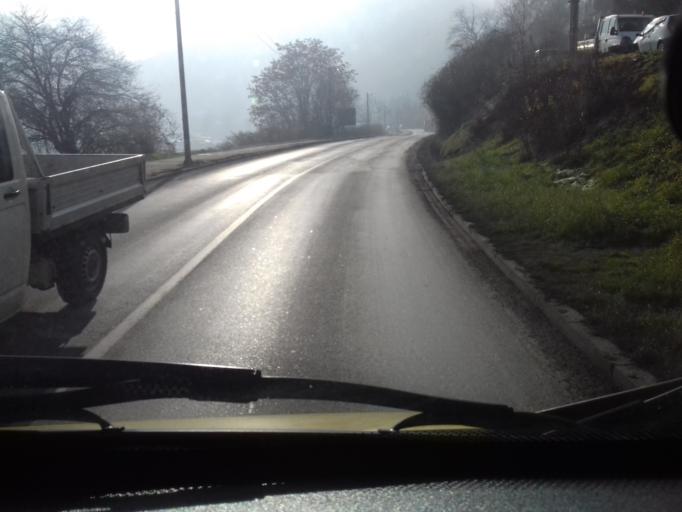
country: BA
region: Federation of Bosnia and Herzegovina
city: Zenica
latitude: 44.1909
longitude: 17.9188
